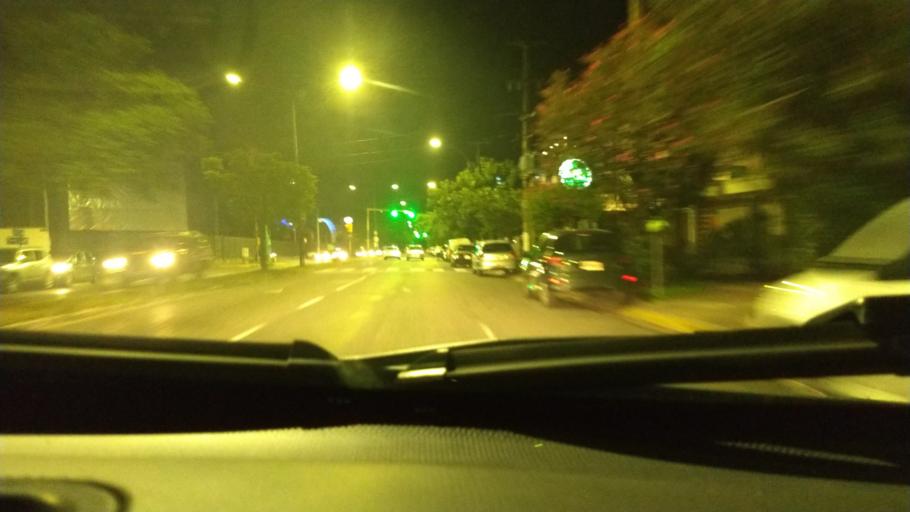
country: AR
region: Cordoba
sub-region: Departamento de Capital
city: Cordoba
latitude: -31.3619
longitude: -64.2376
